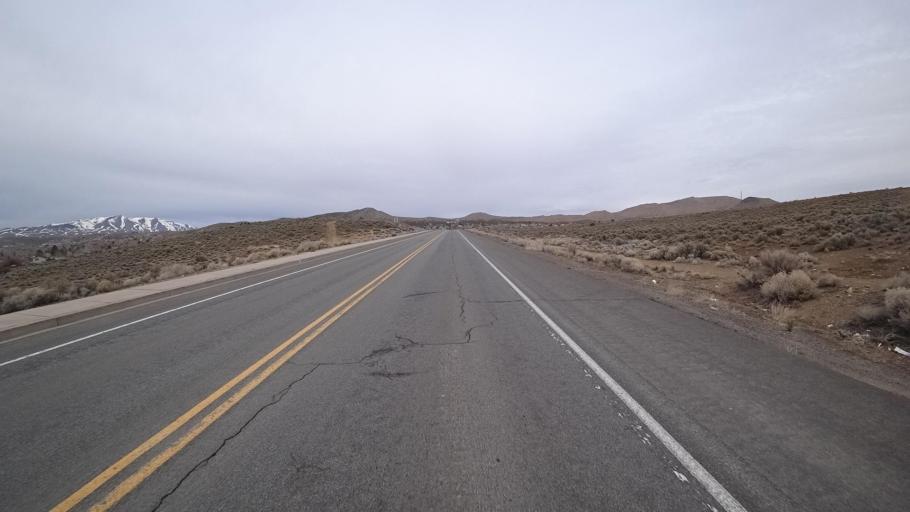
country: US
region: Nevada
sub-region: Washoe County
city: Sun Valley
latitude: 39.6086
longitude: -119.7589
